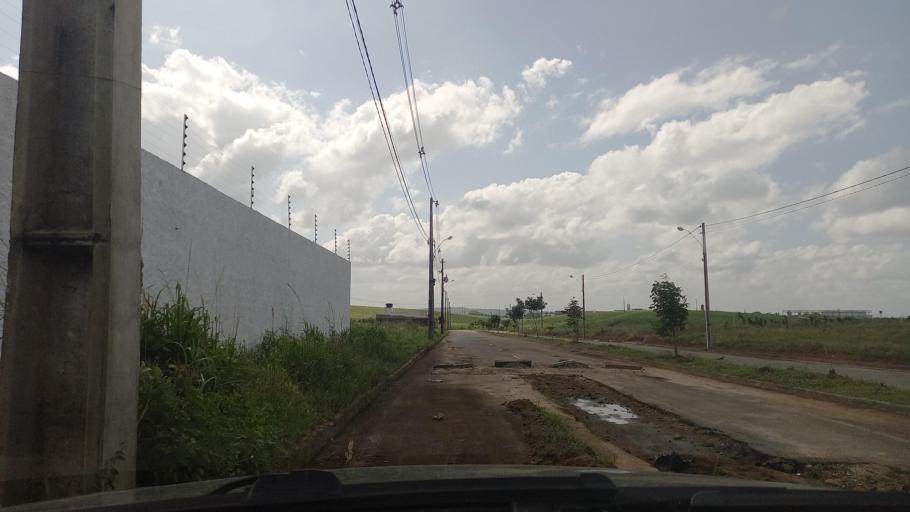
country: BR
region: Pernambuco
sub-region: Goiana
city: Goiana
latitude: -7.5661
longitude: -35.0326
